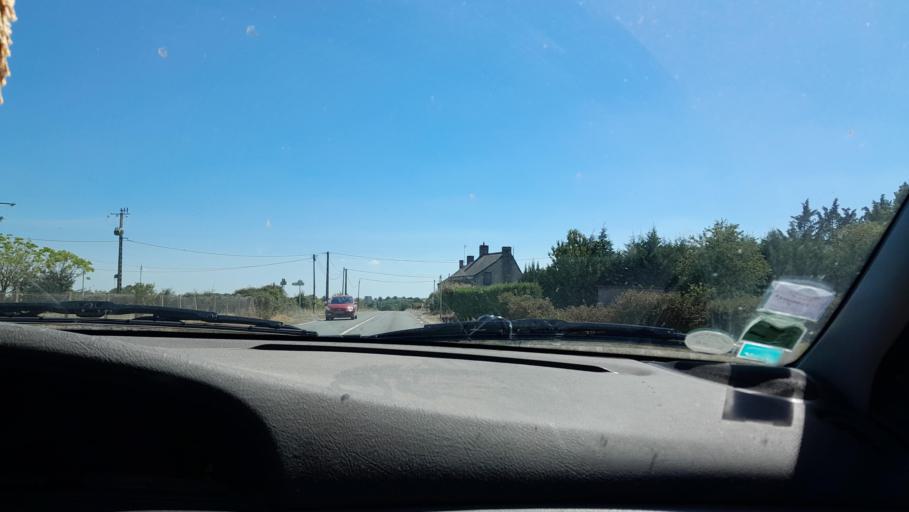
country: FR
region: Pays de la Loire
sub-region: Departement de la Loire-Atlantique
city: Saint-Mars-la-Jaille
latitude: 47.5745
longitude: -1.1899
